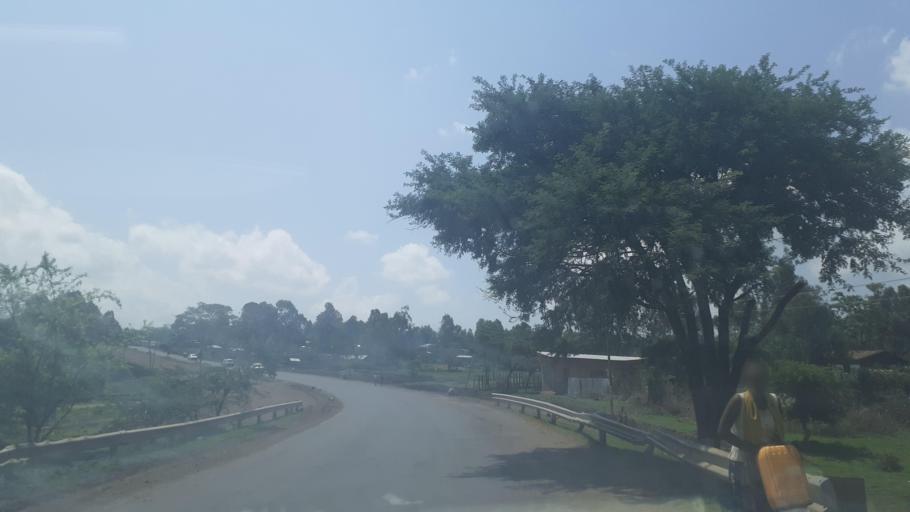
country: ET
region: Oromiya
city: Guder
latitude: 8.9899
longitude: 37.7995
